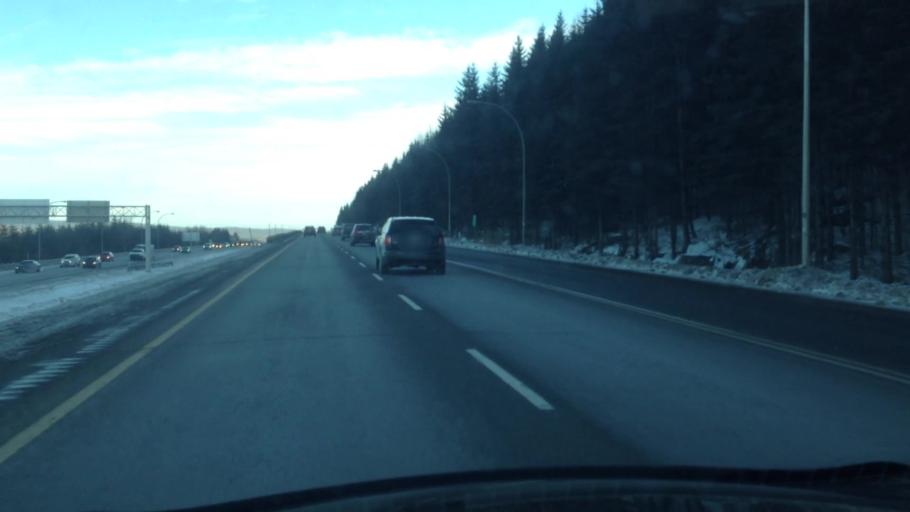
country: CA
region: Quebec
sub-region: Laurentides
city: Prevost
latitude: 45.8825
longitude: -74.1037
